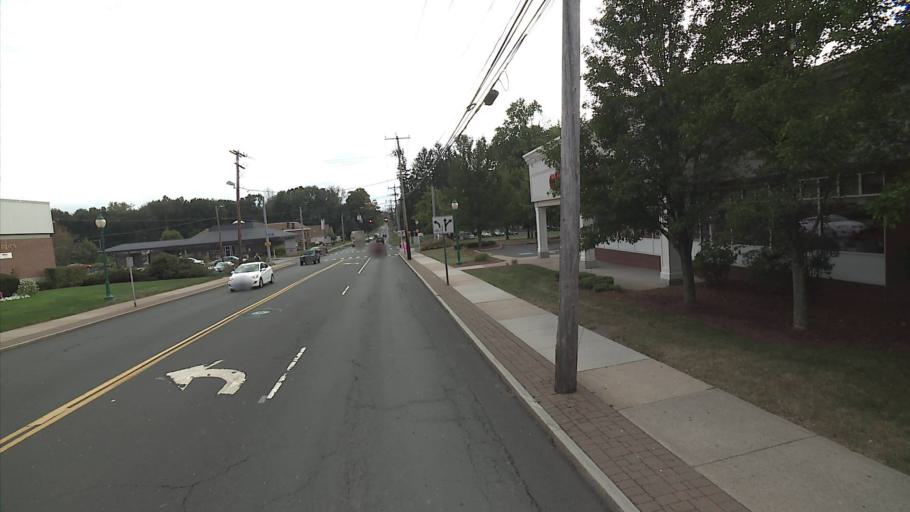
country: US
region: Connecticut
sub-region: Hartford County
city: Newington
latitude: 41.6958
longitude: -72.7229
